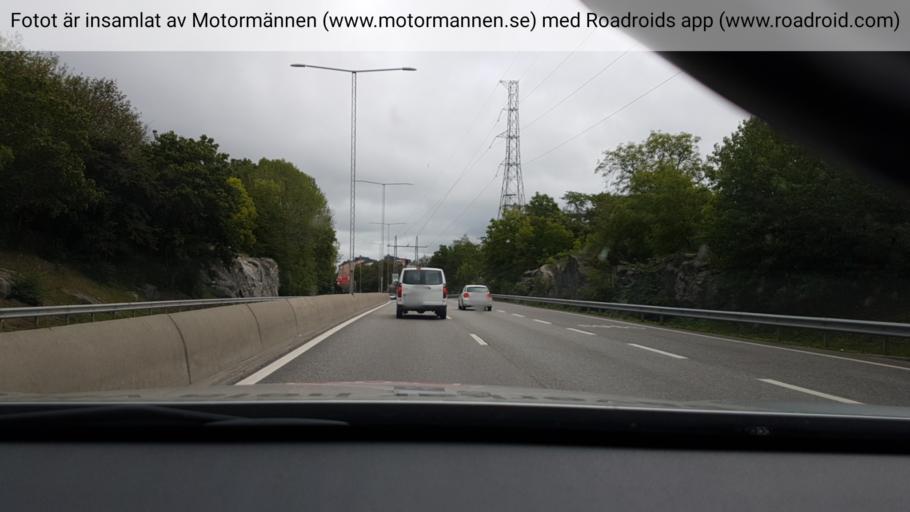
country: SE
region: Stockholm
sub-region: Stockholms Kommun
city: Arsta
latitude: 59.2812
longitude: 18.0398
